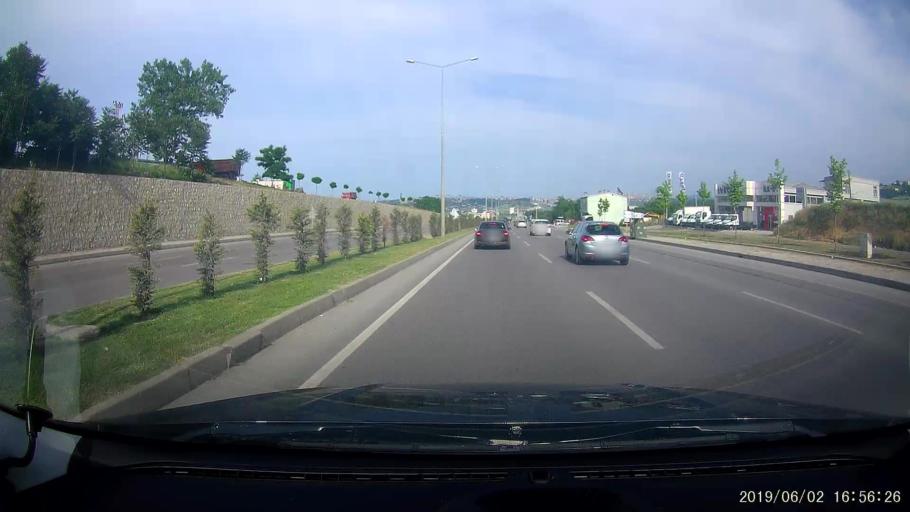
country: TR
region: Samsun
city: Samsun
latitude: 41.2927
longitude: 36.2598
